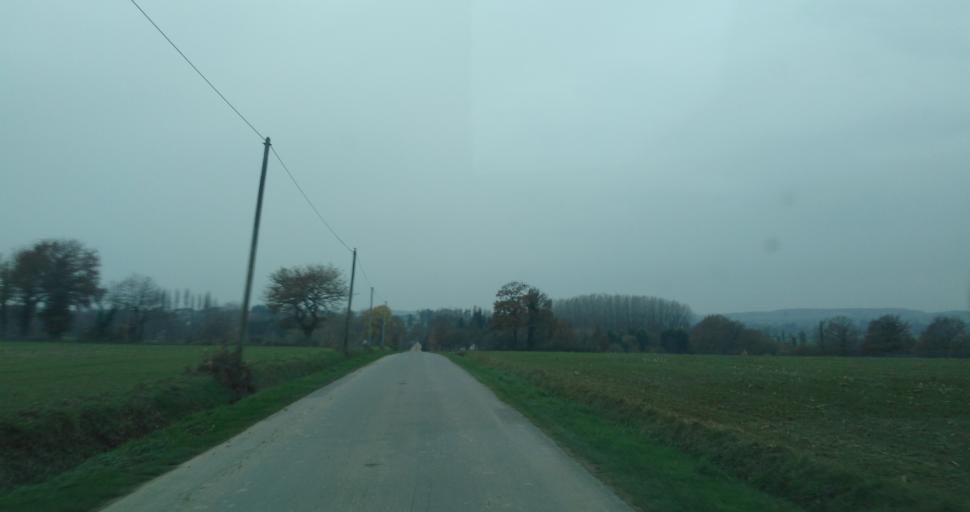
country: FR
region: Brittany
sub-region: Departement d'Ille-et-Vilaine
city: Iffendic
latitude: 48.0944
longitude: -2.0879
